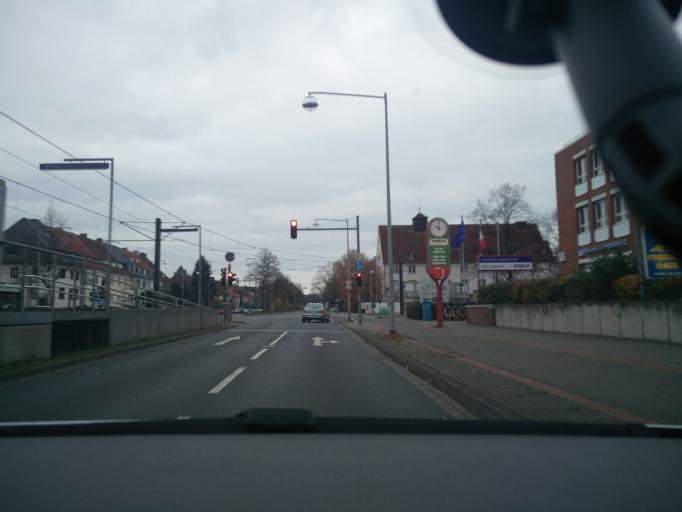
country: DE
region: Lower Saxony
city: Hannover
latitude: 52.3646
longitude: 9.7731
